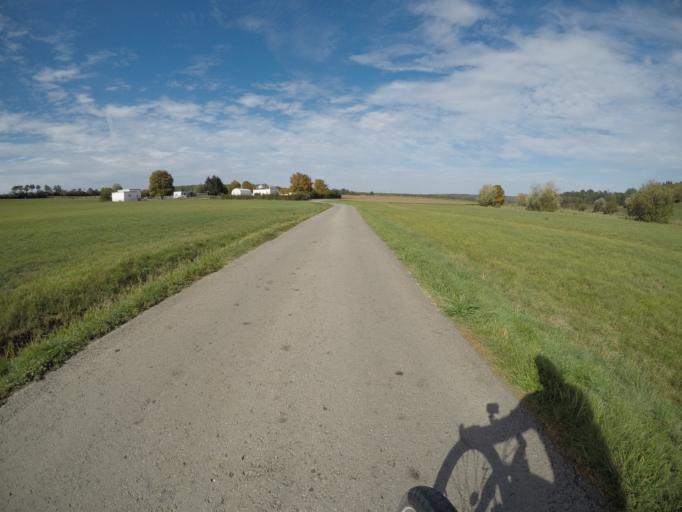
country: DE
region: Baden-Wuerttemberg
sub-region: Regierungsbezirk Stuttgart
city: Hildrizhausen
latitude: 48.6317
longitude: 8.9794
